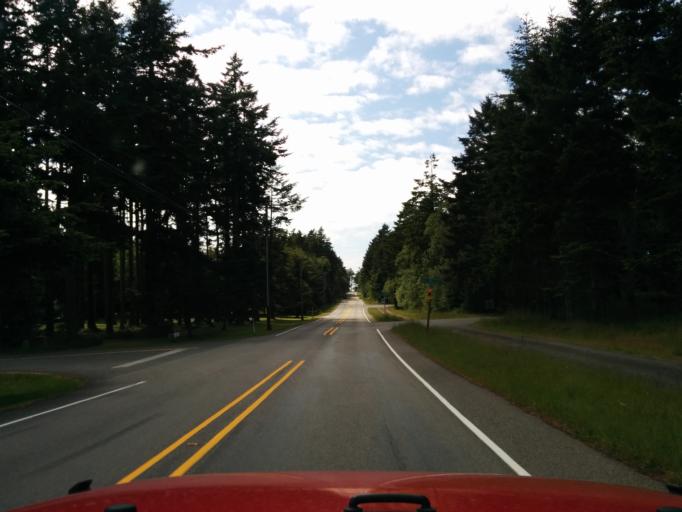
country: US
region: Washington
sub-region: Island County
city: Coupeville
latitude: 48.2319
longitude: -122.7579
